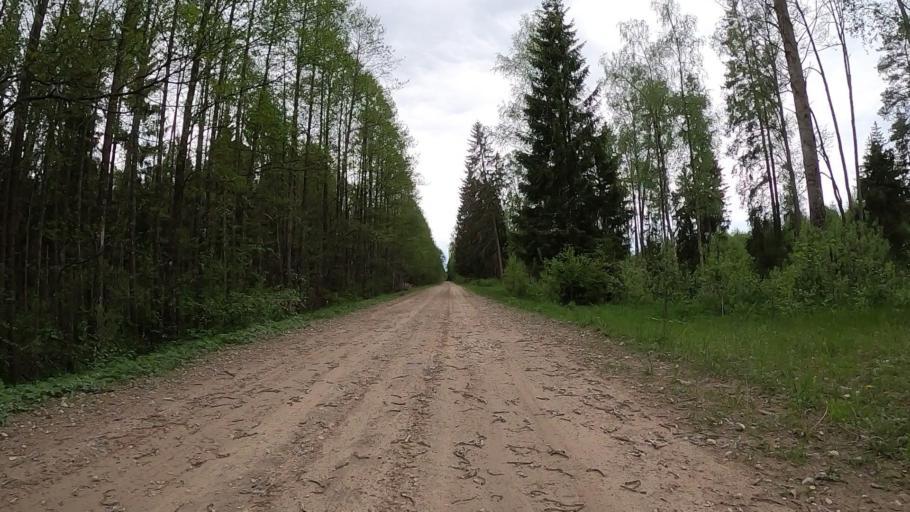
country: LV
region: Ozolnieku
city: Ozolnieki
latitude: 56.7773
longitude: 23.7679
